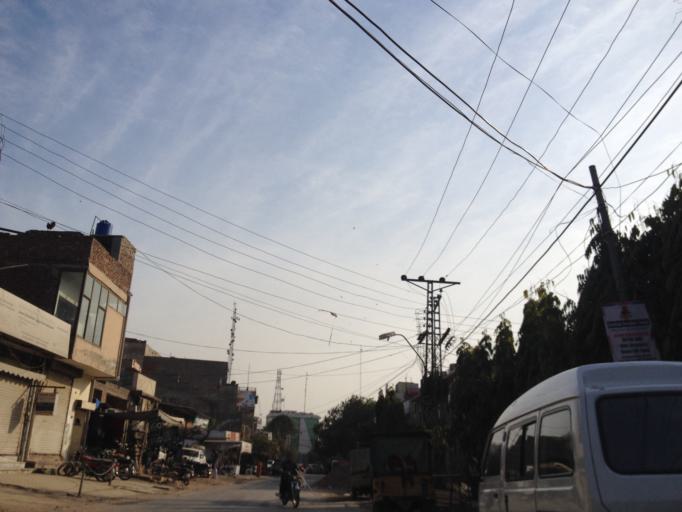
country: PK
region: Punjab
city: Lahore
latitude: 31.5037
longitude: 74.3189
